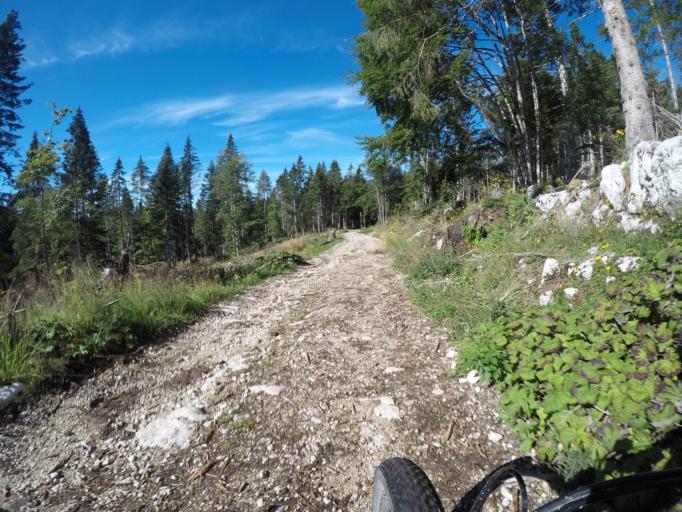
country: IT
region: Veneto
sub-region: Provincia di Vicenza
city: Asiago
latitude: 45.9109
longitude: 11.4840
